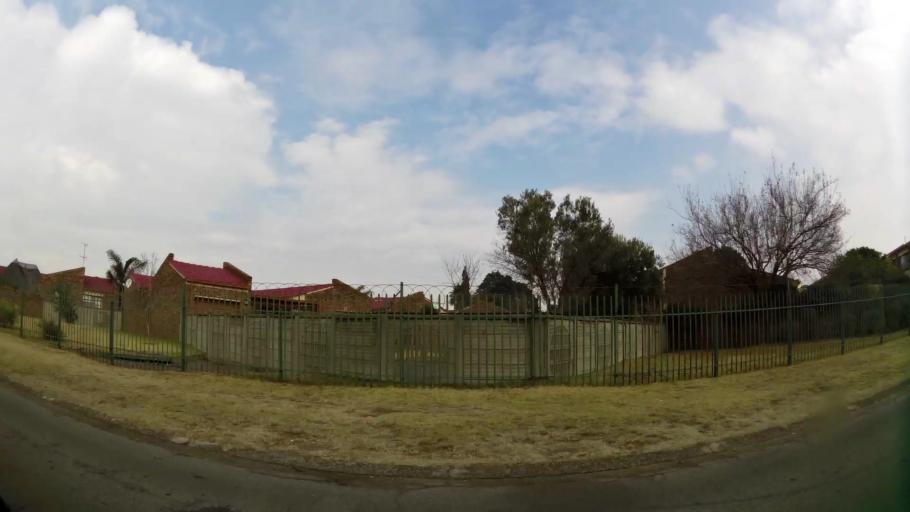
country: ZA
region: Gauteng
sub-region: Sedibeng District Municipality
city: Vanderbijlpark
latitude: -26.6930
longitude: 27.8500
